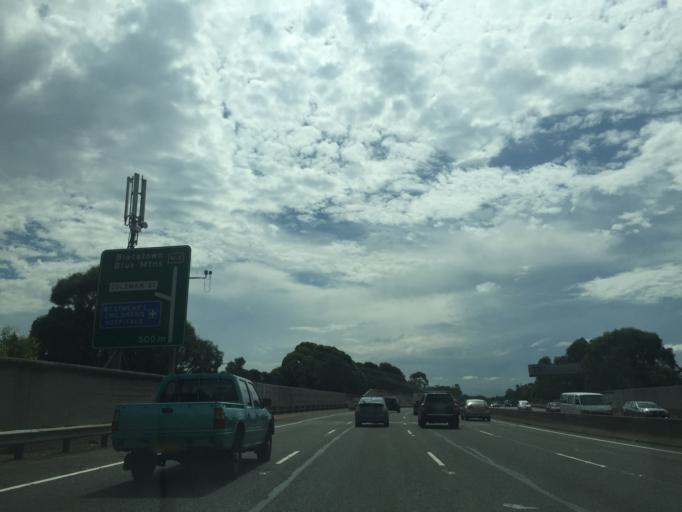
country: AU
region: New South Wales
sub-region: Holroyd
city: Merrylands
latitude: -33.8246
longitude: 150.9886
